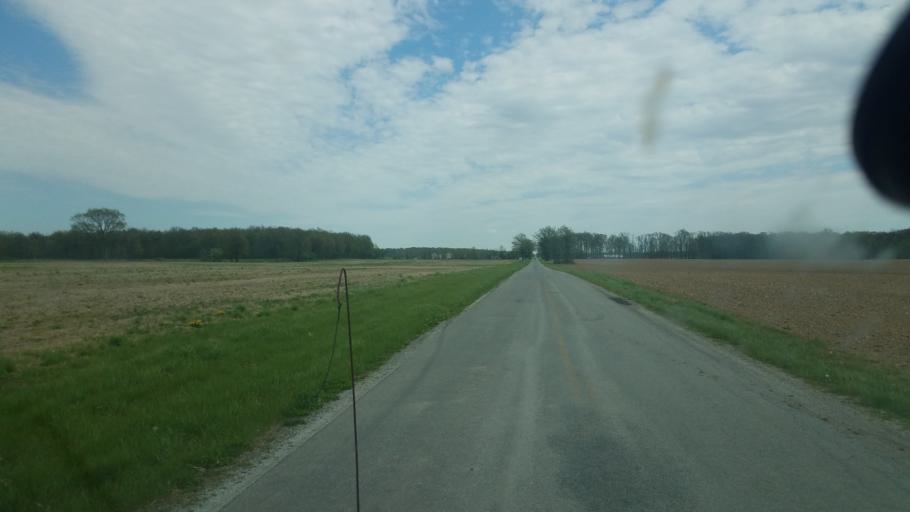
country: US
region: Ohio
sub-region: Allen County
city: Bluffton
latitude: 40.8199
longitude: -83.8800
